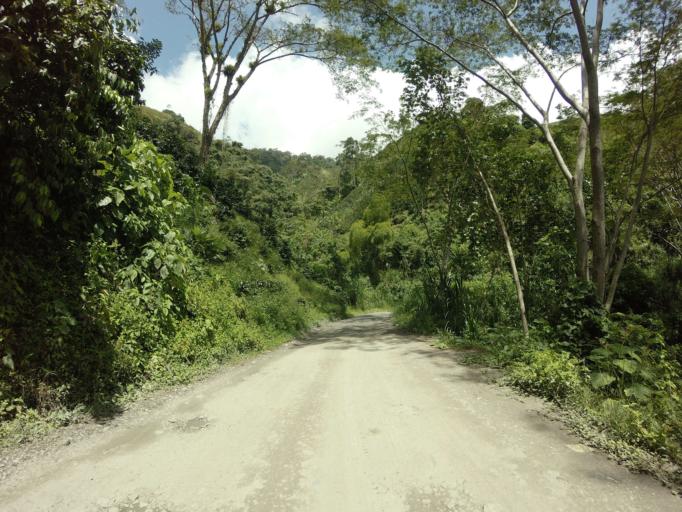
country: CO
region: Caldas
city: Marquetalia
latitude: 5.2917
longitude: -75.0960
